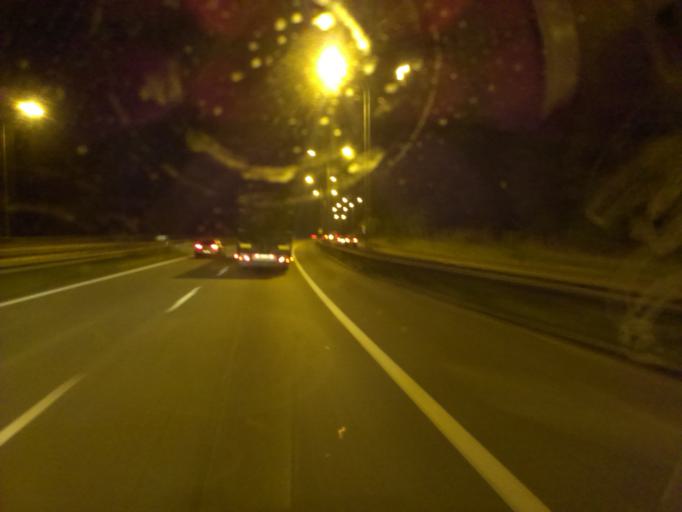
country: PL
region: Silesian Voivodeship
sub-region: Katowice
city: Katowice
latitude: 50.2379
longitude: 19.0594
